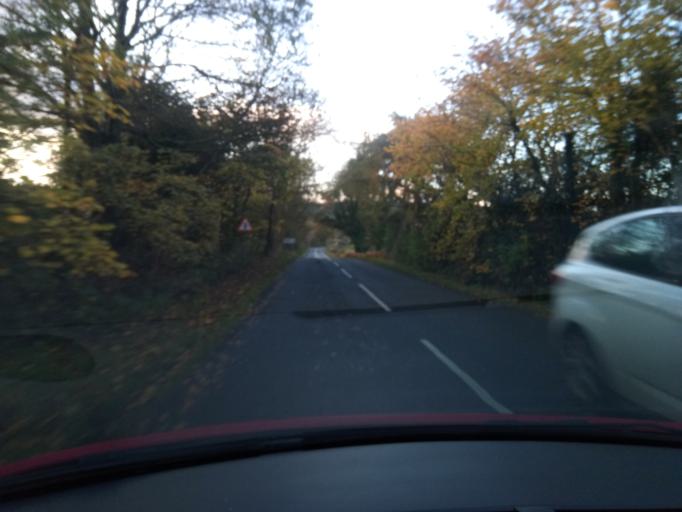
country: GB
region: England
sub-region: County Durham
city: Hamsterley
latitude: 54.6774
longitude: -1.8300
